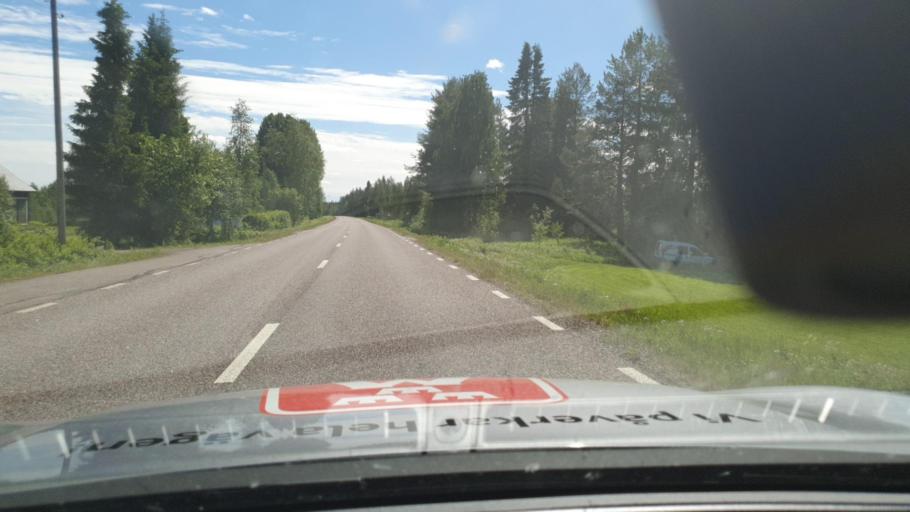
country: FI
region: Lapland
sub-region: Torniolaakso
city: Pello
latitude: 66.9287
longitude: 23.8507
